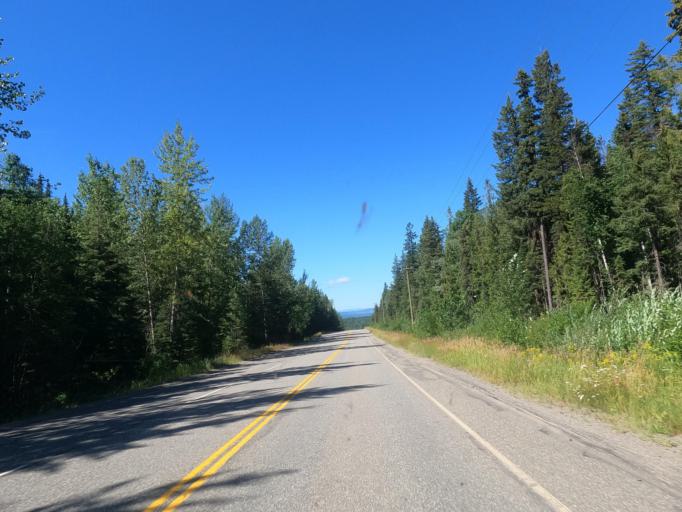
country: CA
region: British Columbia
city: Quesnel
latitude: 53.0246
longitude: -122.3479
